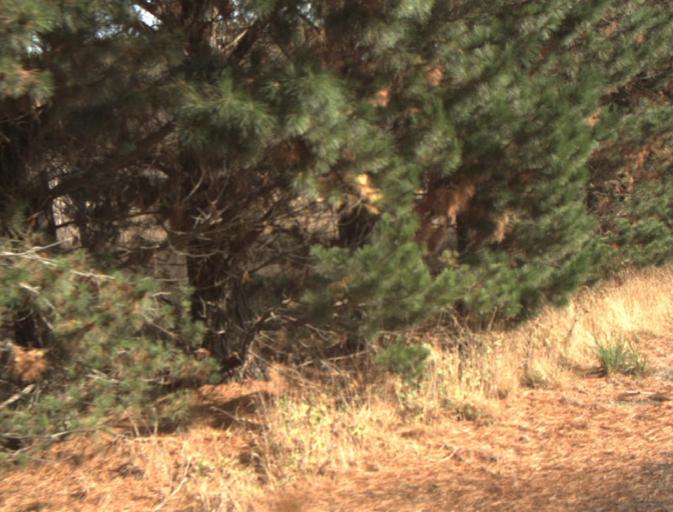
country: AU
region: Tasmania
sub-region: Launceston
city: Mayfield
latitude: -41.2117
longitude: 147.1815
